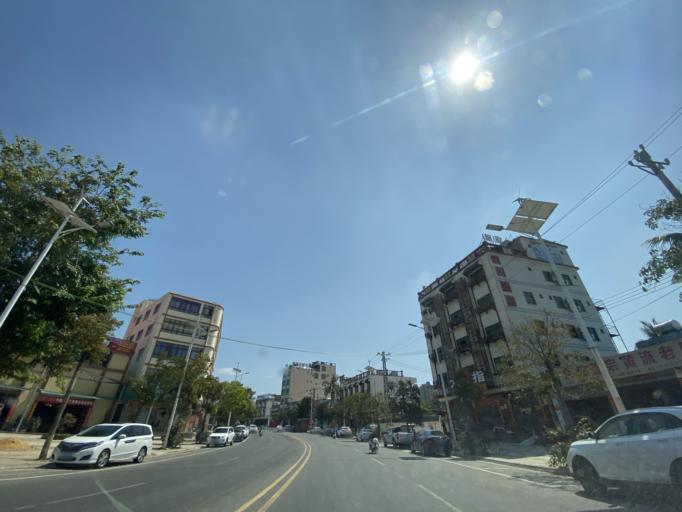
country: CN
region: Hainan
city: Yingzhou
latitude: 18.4224
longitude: 109.8469
